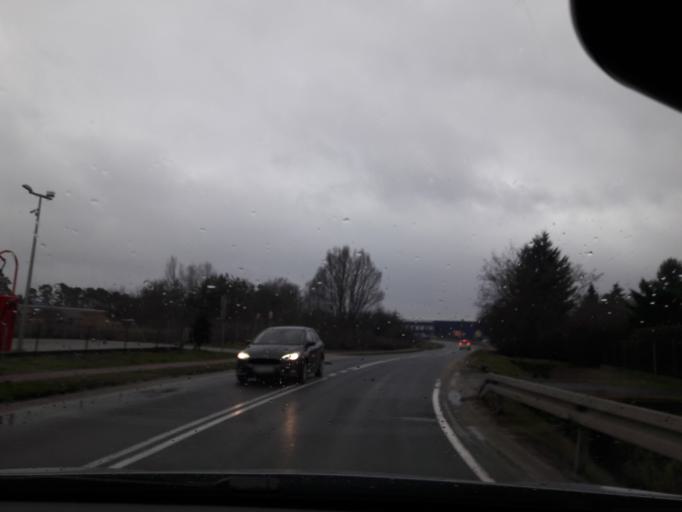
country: PL
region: Greater Poland Voivodeship
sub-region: Powiat poznanski
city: Suchy Las
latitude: 52.4707
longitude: 16.8752
